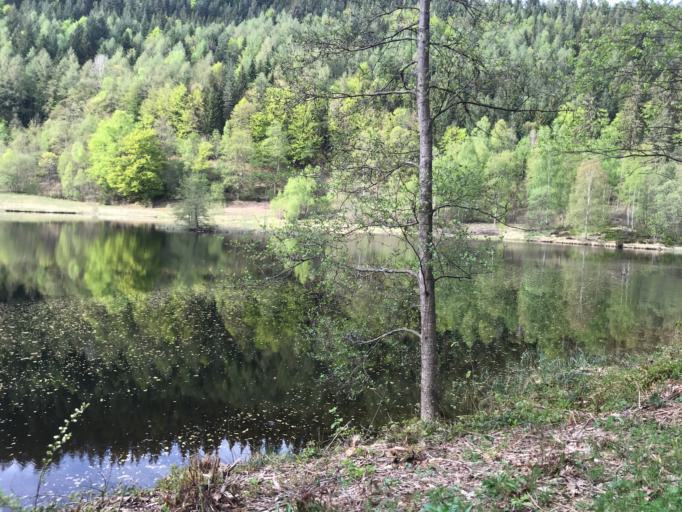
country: DE
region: Baden-Wuerttemberg
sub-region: Karlsruhe Region
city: Baiersbronn
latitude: 48.4833
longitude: 8.3389
